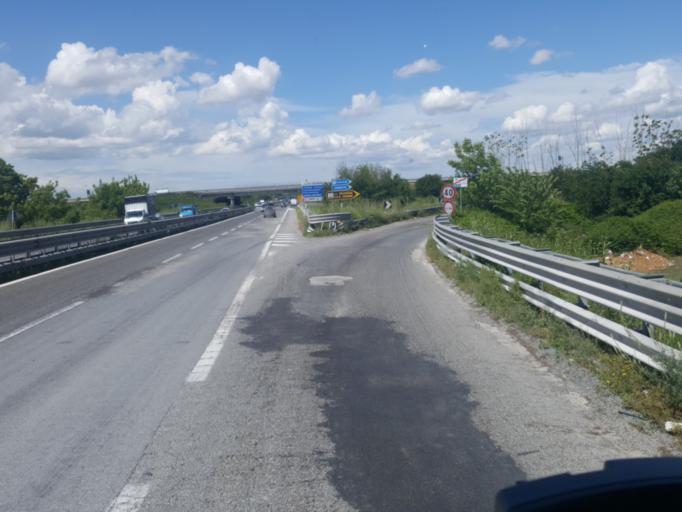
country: IT
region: Campania
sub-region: Provincia di Napoli
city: Pascarola
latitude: 40.9735
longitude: 14.2968
